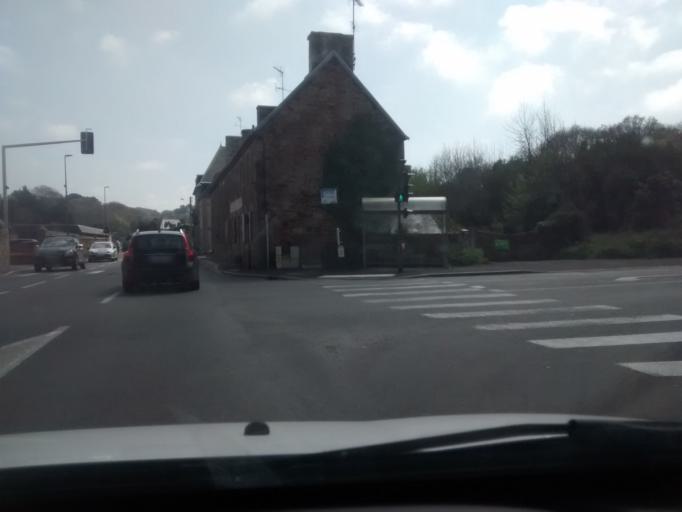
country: FR
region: Brittany
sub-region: Departement des Cotes-d'Armor
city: Perros-Guirec
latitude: 48.7993
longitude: -3.4423
